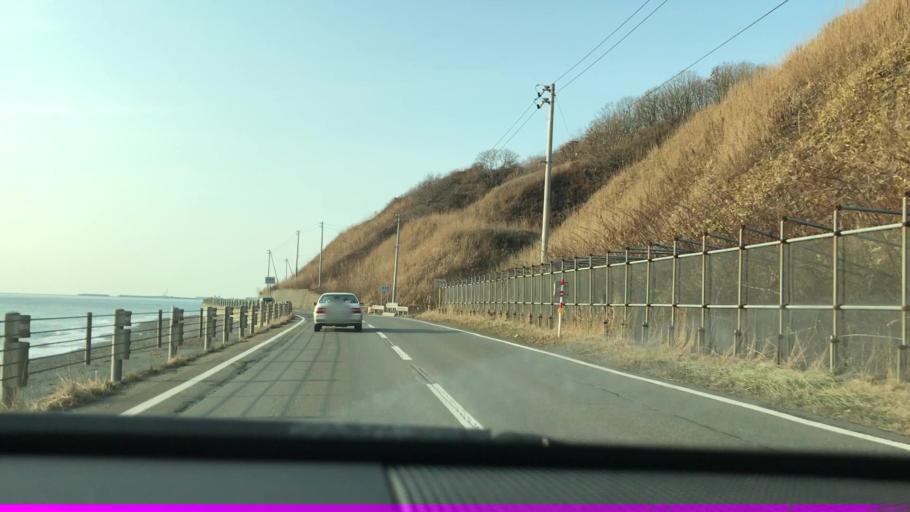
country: JP
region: Hokkaido
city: Shizunai-furukawacho
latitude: 42.2364
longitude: 142.5976
